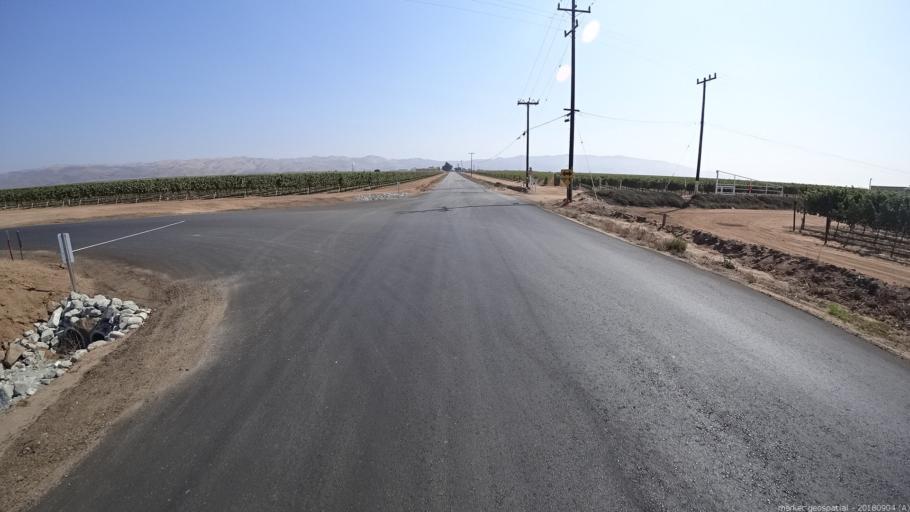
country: US
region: California
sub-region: Monterey County
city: Gonzales
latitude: 36.5016
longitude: -121.3953
